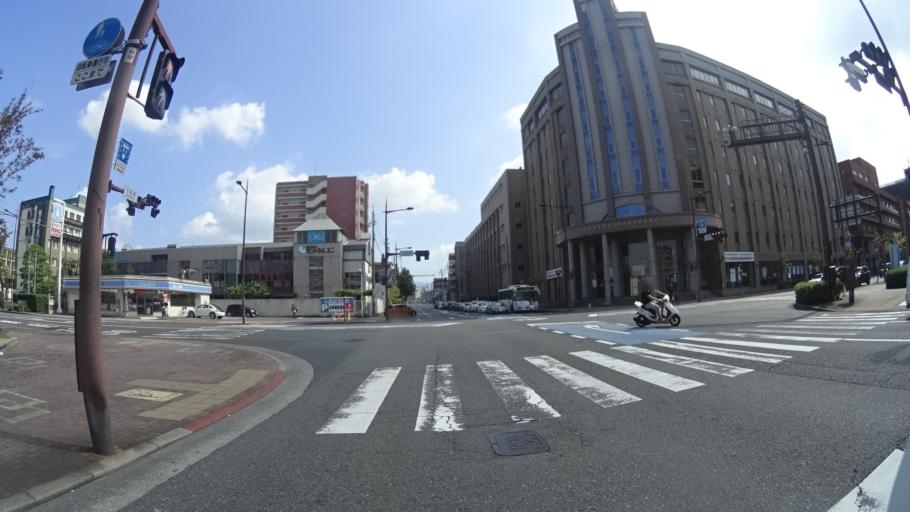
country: JP
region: Fukuoka
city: Kitakyushu
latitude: 33.8778
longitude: 130.8581
